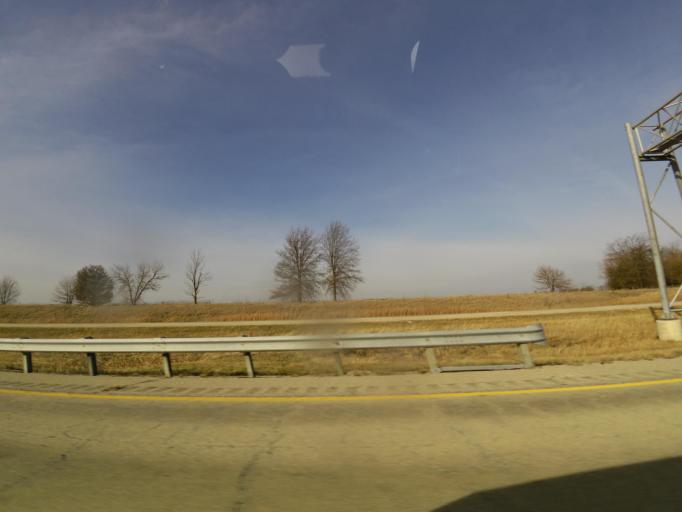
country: US
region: Illinois
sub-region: Macon County
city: Warrensburg
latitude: 39.8841
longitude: -89.0195
